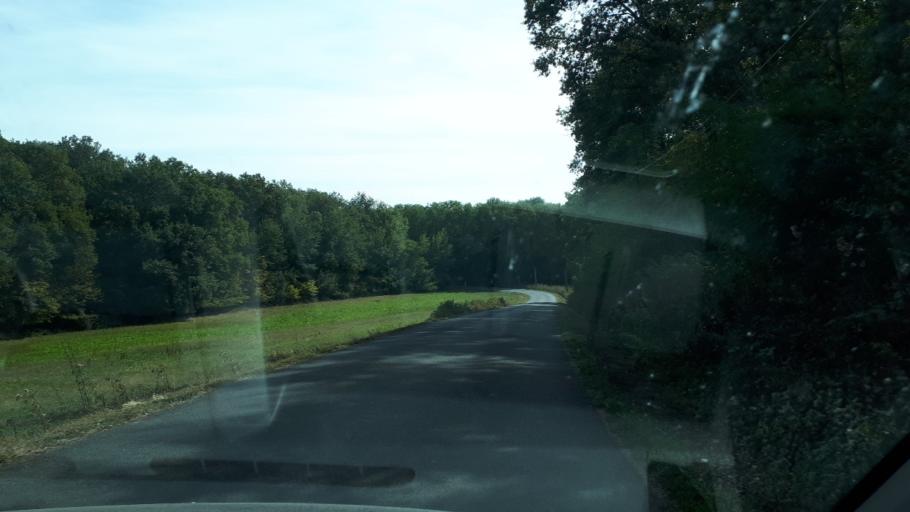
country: FR
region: Centre
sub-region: Departement du Loir-et-Cher
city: Montoire-sur-le-Loir
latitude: 47.7075
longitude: 0.8346
